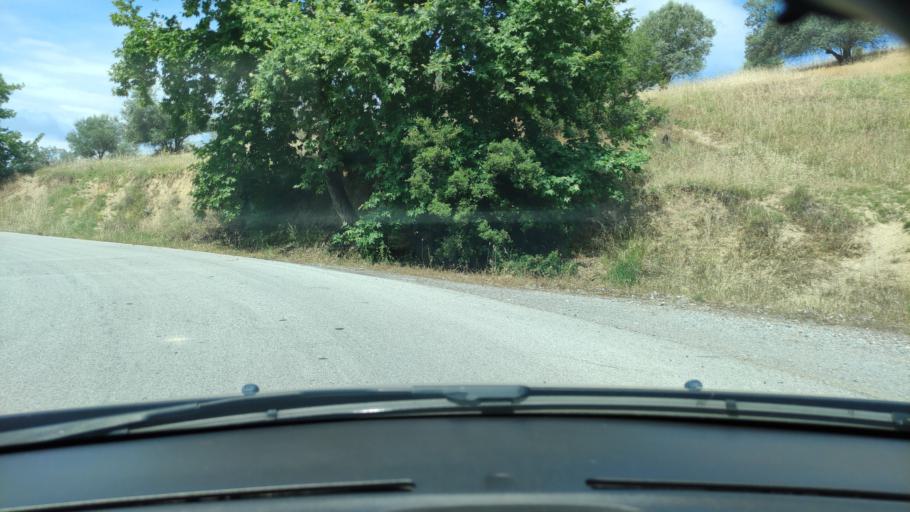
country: GR
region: Central Greece
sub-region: Nomos Evvoias
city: Afration
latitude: 38.5177
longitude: 23.7721
